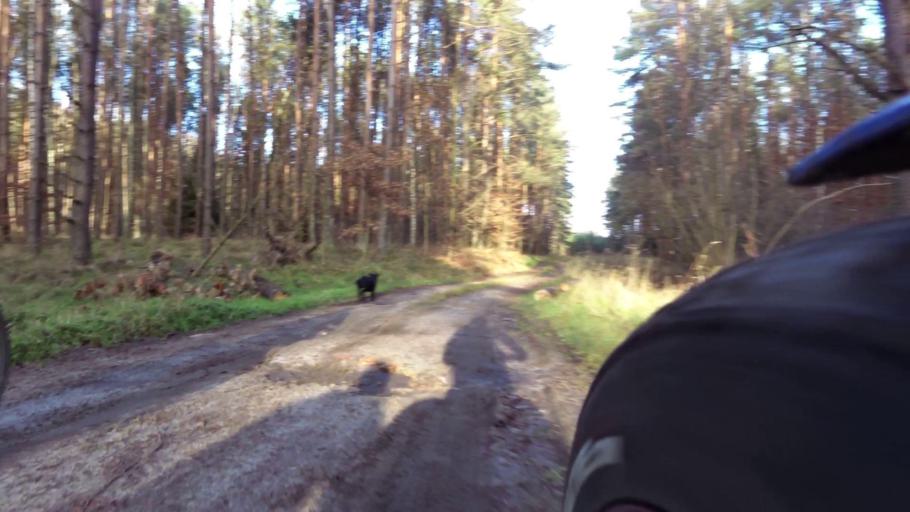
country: PL
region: West Pomeranian Voivodeship
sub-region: Powiat szczecinecki
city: Borne Sulinowo
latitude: 53.6121
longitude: 16.6173
